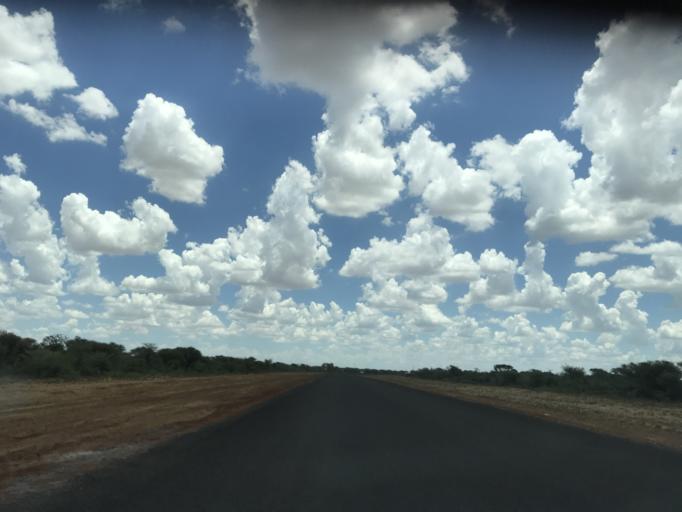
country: BW
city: Mabuli
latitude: -25.8054
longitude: 24.6810
